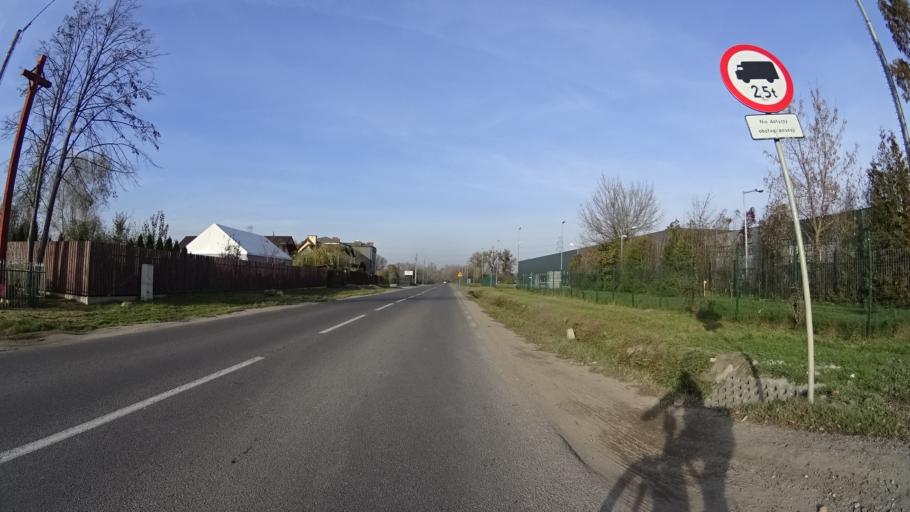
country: PL
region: Masovian Voivodeship
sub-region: Powiat warszawski zachodni
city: Babice
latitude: 52.2821
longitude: 20.8670
